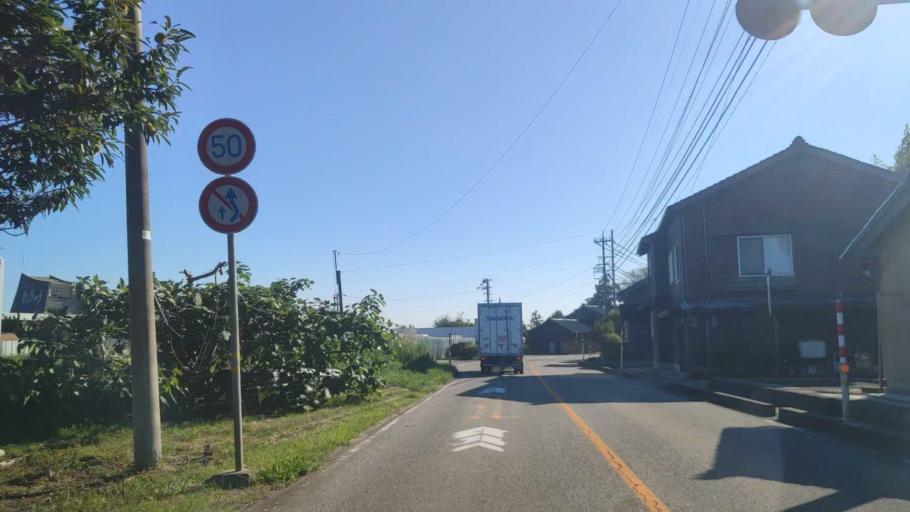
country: JP
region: Ishikawa
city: Nanao
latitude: 37.1936
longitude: 136.9107
